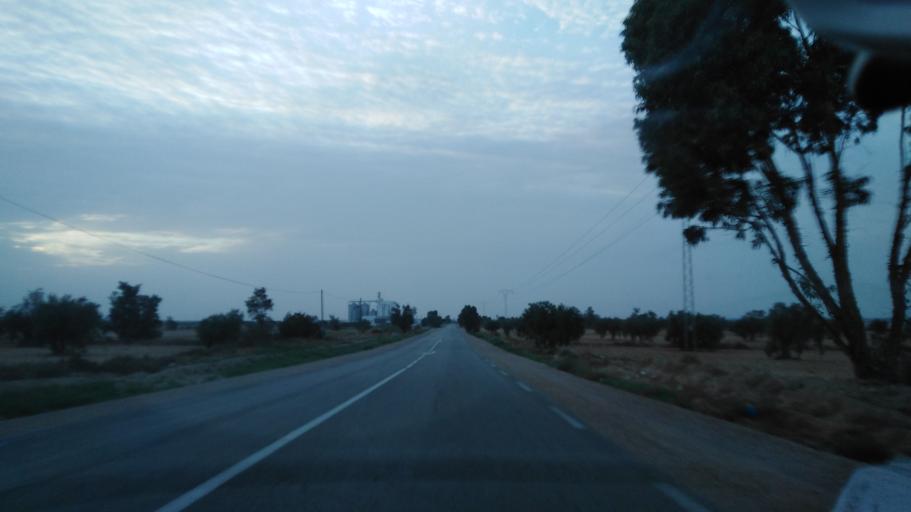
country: TN
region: Al Mahdiyah
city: Shurban
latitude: 34.9468
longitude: 10.4044
